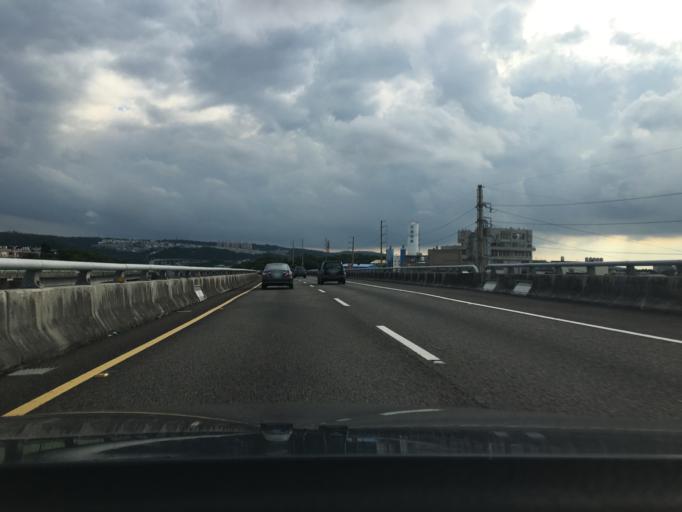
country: TW
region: Taiwan
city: Daxi
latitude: 24.9241
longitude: 121.1700
